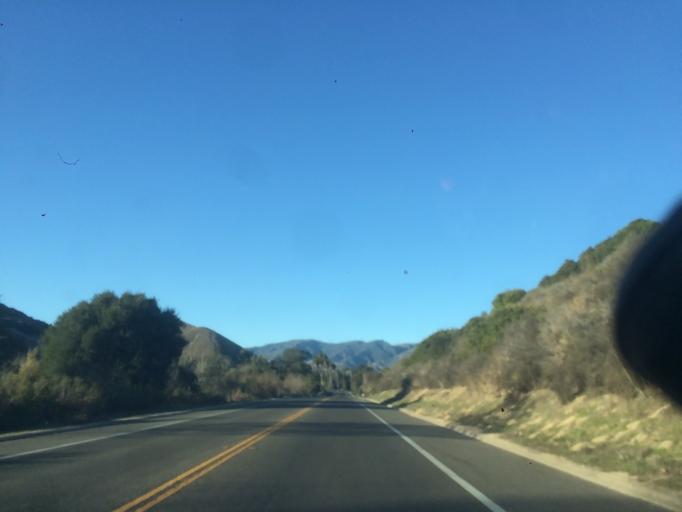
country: US
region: California
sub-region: Santa Barbara County
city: Santa Barbara
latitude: 34.4064
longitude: -119.7395
